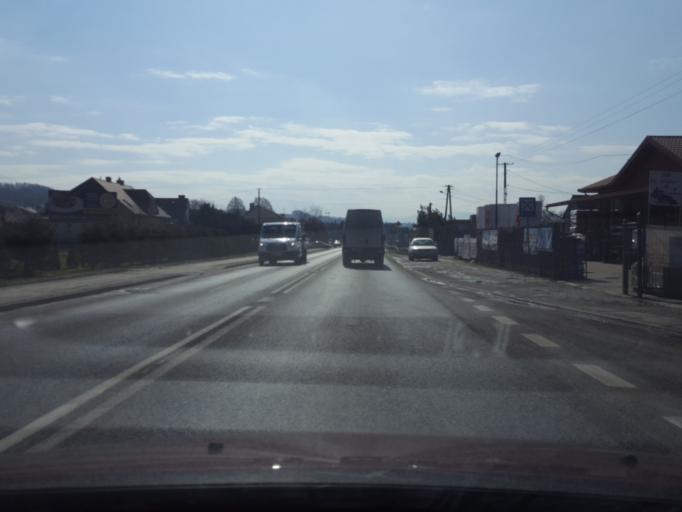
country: PL
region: Lesser Poland Voivodeship
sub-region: Powiat nowosadecki
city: Chelmiec
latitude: 49.6737
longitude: 20.6840
